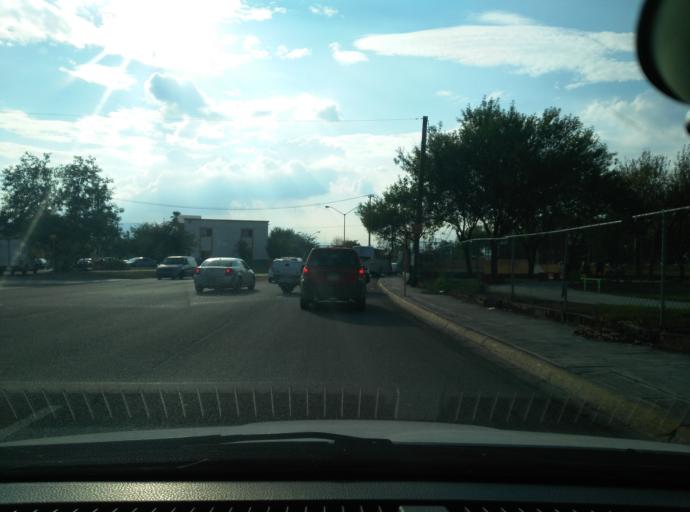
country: MX
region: Nuevo Leon
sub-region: Apodaca
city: Fraccionamiento Cosmopolis Octavo Sector
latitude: 25.7689
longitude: -100.2480
